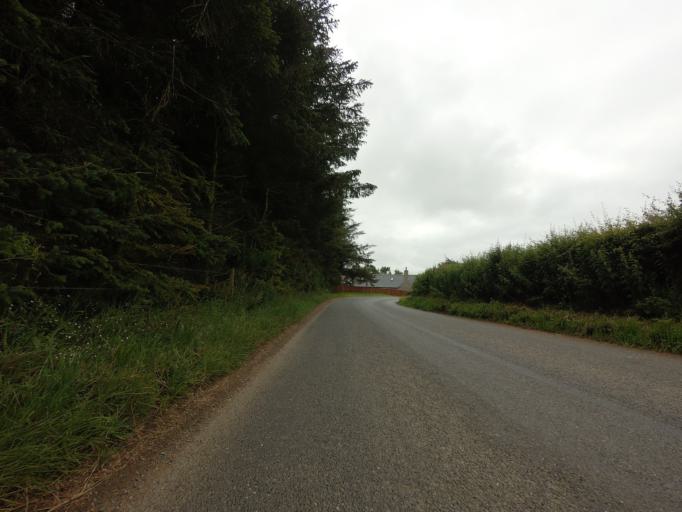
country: GB
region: Scotland
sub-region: Aberdeenshire
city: Rosehearty
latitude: 57.5399
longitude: -2.1894
